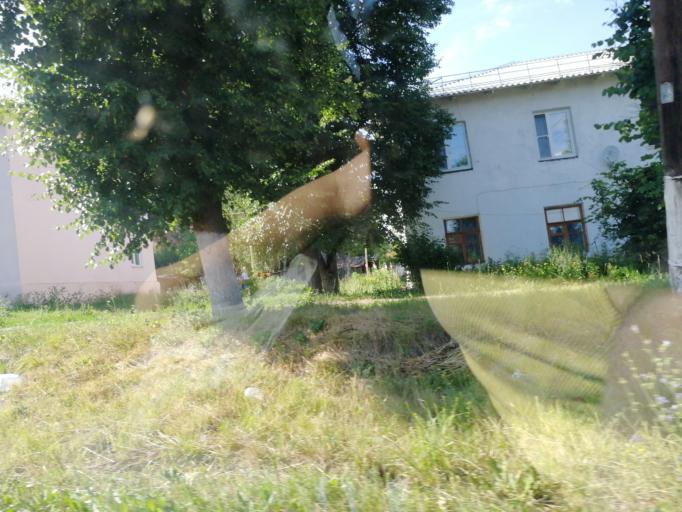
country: RU
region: Tula
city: Bogoroditsk
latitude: 53.7667
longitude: 38.1251
